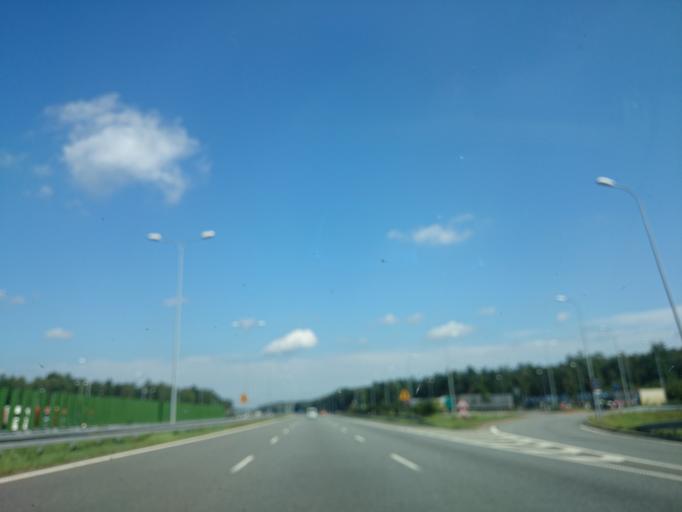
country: PL
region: Silesian Voivodeship
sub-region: Powiat gliwicki
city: Gieraltowice
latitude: 50.1951
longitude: 18.7028
